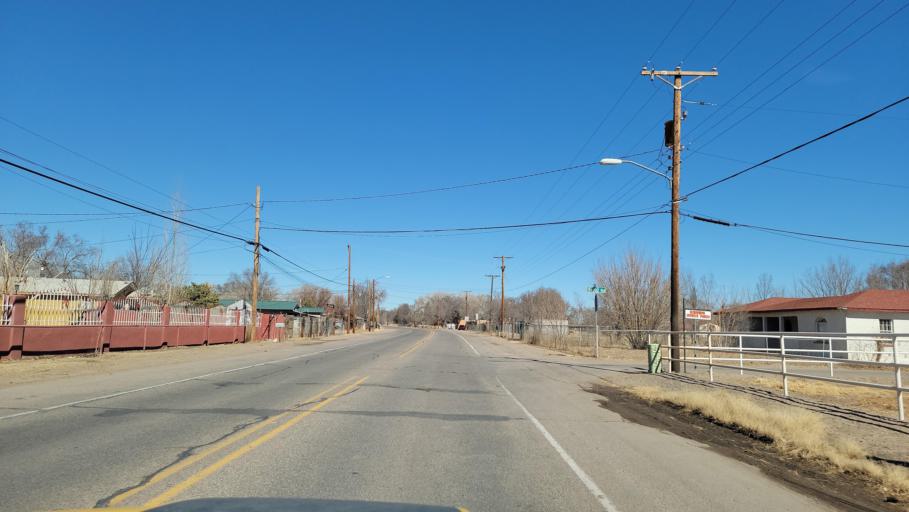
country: US
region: New Mexico
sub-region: Bernalillo County
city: South Valley
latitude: 34.9634
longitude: -106.6955
